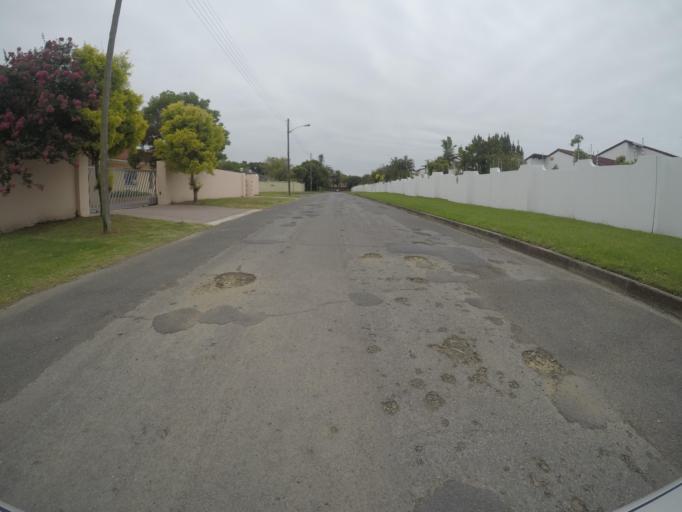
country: ZA
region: Eastern Cape
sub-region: Buffalo City Metropolitan Municipality
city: East London
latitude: -32.9751
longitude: 27.9388
